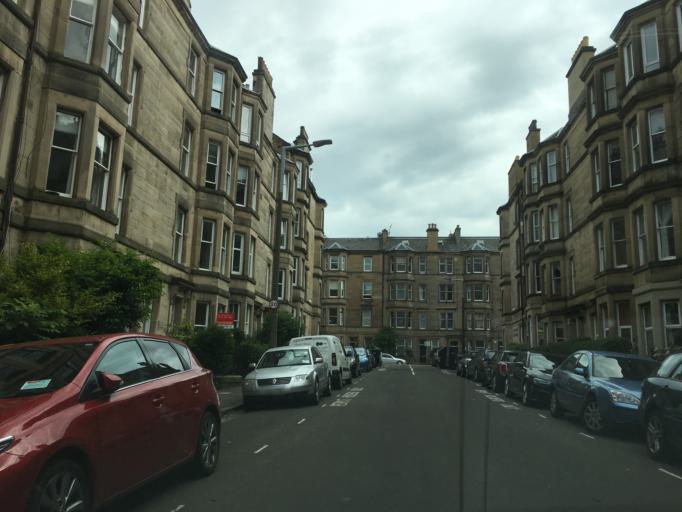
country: GB
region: Scotland
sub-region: Edinburgh
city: Edinburgh
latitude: 55.9375
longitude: -3.2190
